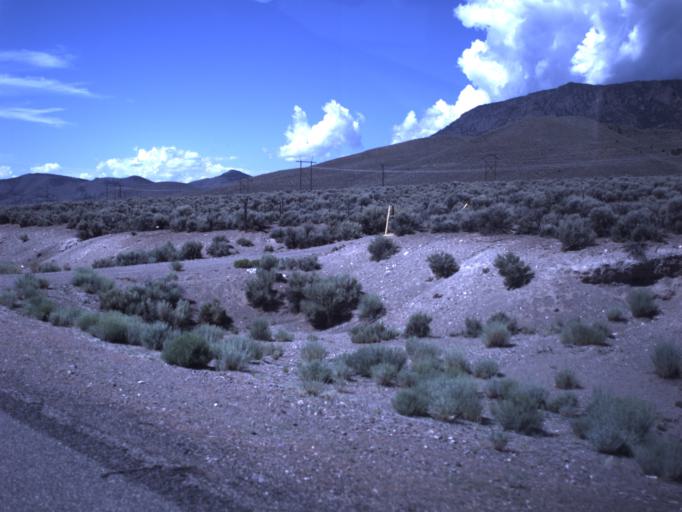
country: US
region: Utah
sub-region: Piute County
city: Junction
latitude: 38.2990
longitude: -112.2247
